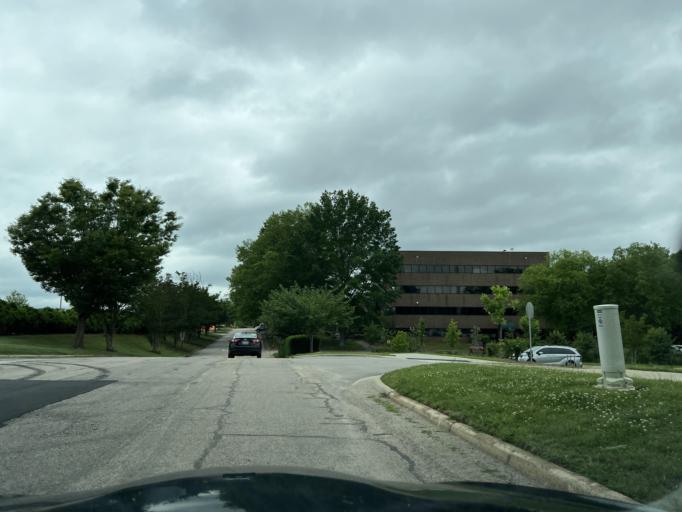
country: US
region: North Carolina
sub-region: Wake County
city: Cary
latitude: 35.7754
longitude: -78.7562
